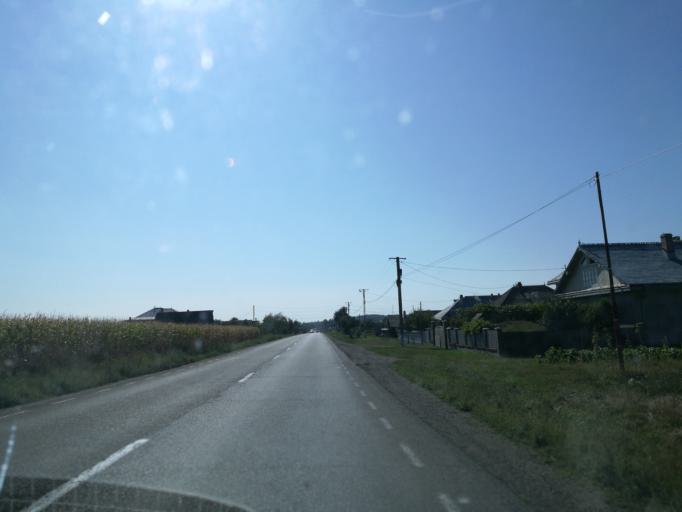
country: RO
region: Suceava
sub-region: Comuna Forasti
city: Oniceni
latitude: 47.3166
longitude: 26.4673
